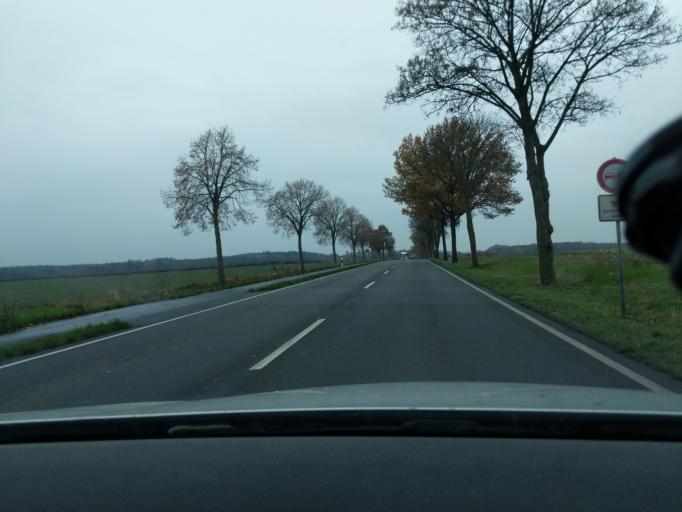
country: DE
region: Lower Saxony
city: Zeven
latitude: 53.2567
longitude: 9.2777
